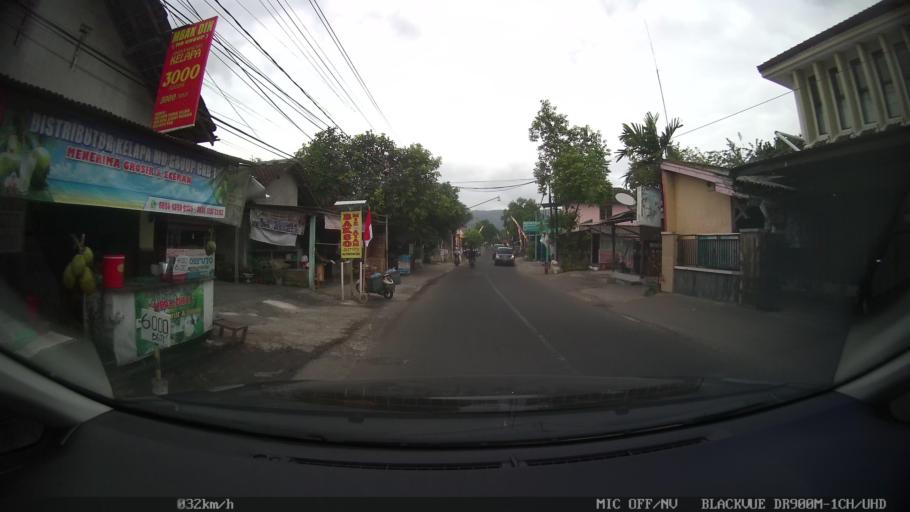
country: ID
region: Daerah Istimewa Yogyakarta
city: Sewon
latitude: -7.8779
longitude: 110.4113
